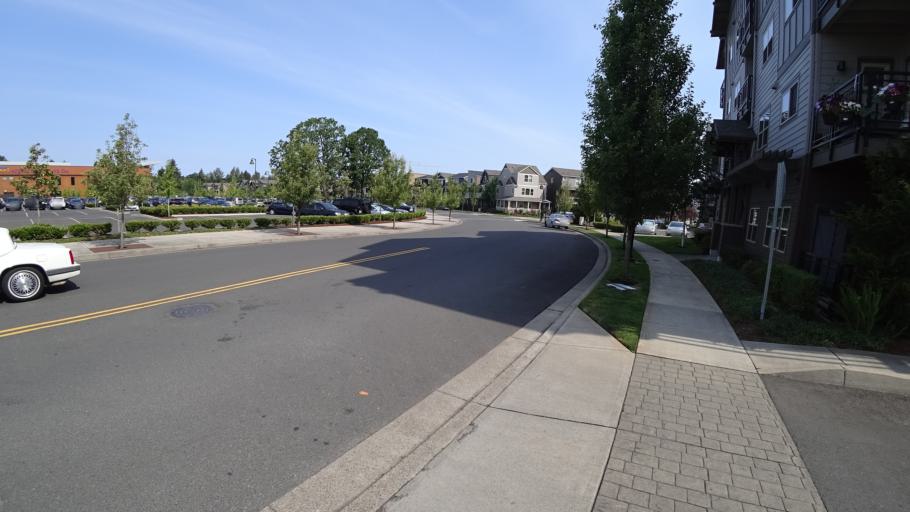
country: US
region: Oregon
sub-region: Washington County
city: Cedar Hills
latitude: 45.5033
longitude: -122.8227
